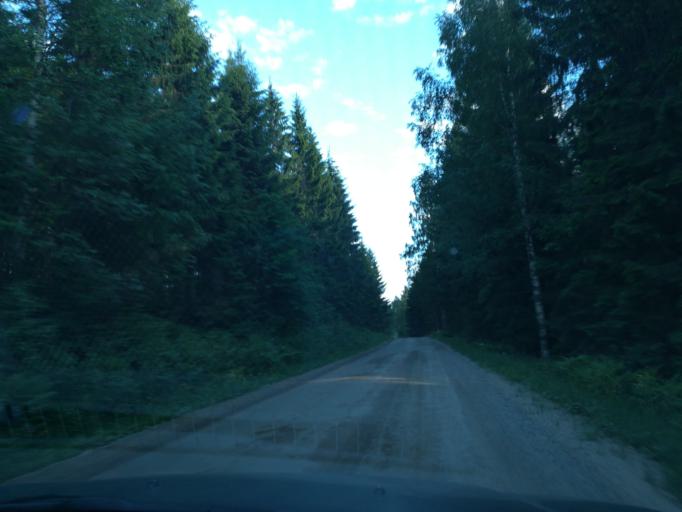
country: FI
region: Southern Savonia
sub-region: Mikkeli
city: Puumala
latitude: 61.6101
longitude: 28.1154
